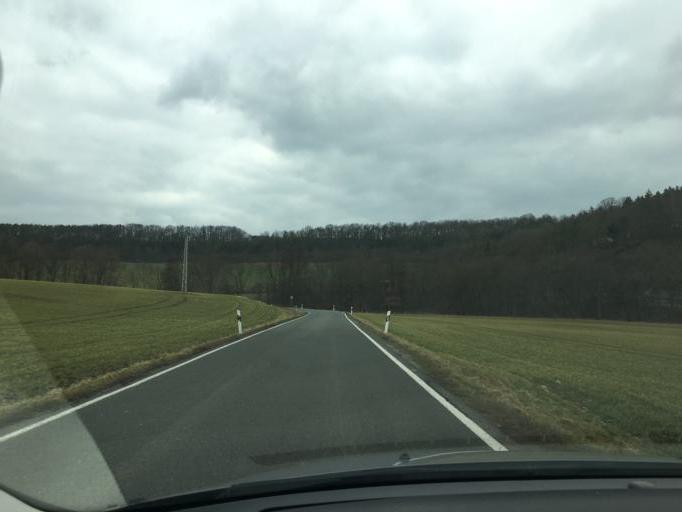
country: DE
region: Thuringia
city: Oettern
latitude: 50.9239
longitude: 11.3558
